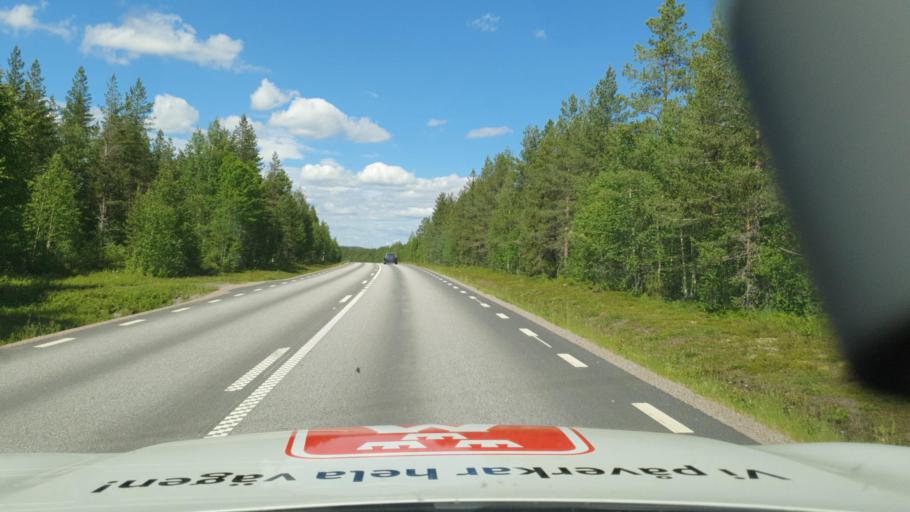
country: SE
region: Vaesterbotten
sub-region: Skelleftea Kommun
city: Langsele
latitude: 64.9835
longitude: 20.2284
